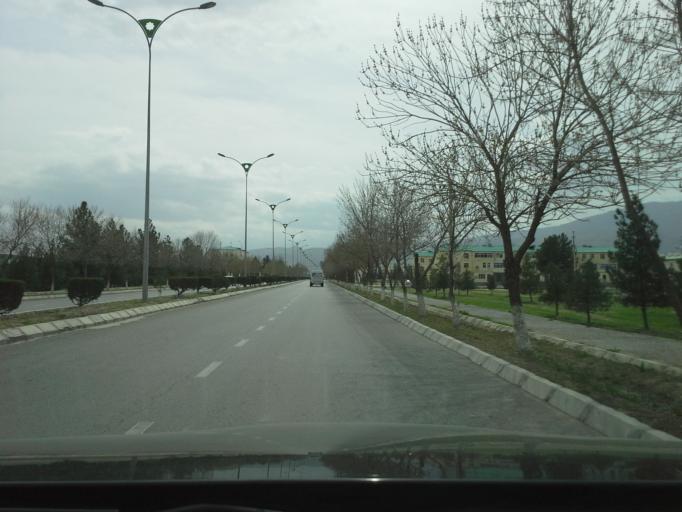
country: TM
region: Ahal
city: Abadan
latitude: 38.0596
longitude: 58.1586
